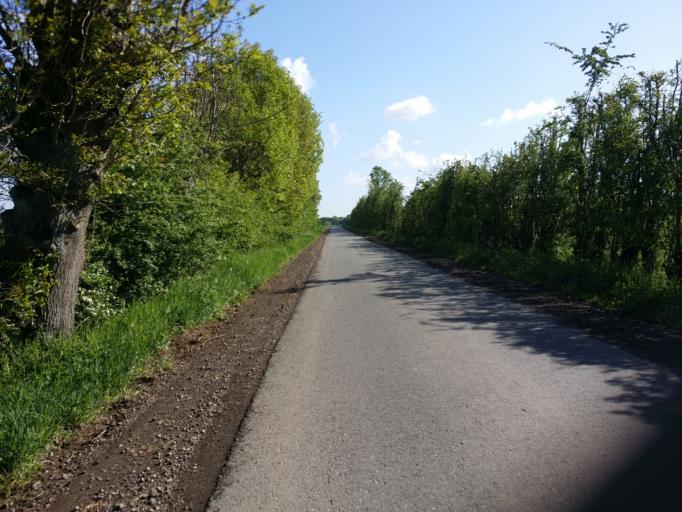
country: DE
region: Lower Saxony
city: Ahsen-Oetzen
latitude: 52.9660
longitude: 9.1110
